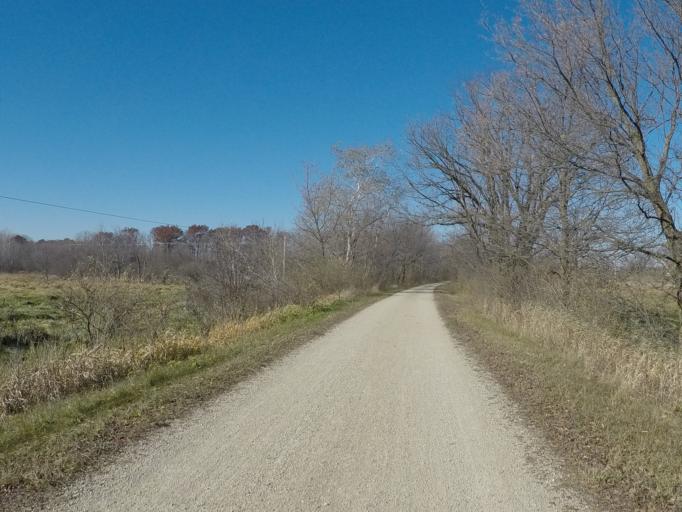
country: US
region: Wisconsin
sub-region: Dane County
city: Deerfield
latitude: 43.0428
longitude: -89.0470
